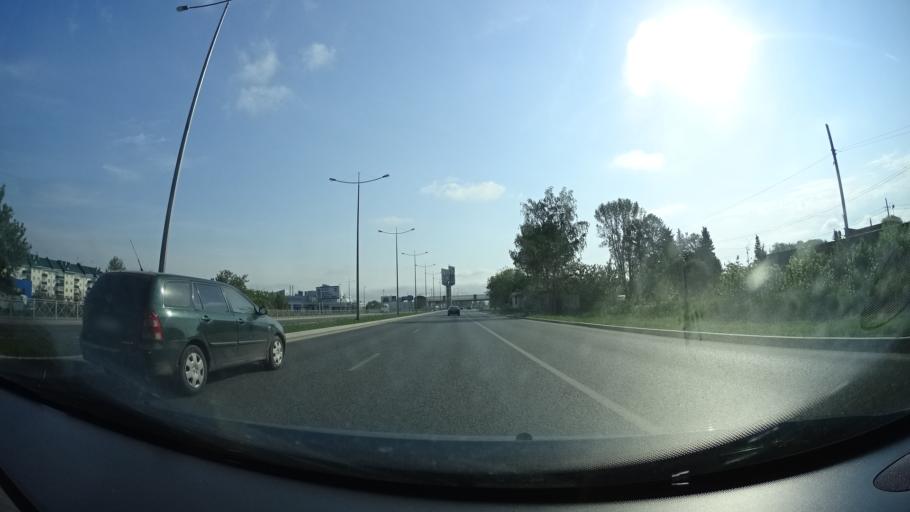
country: RU
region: Perm
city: Kondratovo
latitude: 57.9448
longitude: 56.0769
